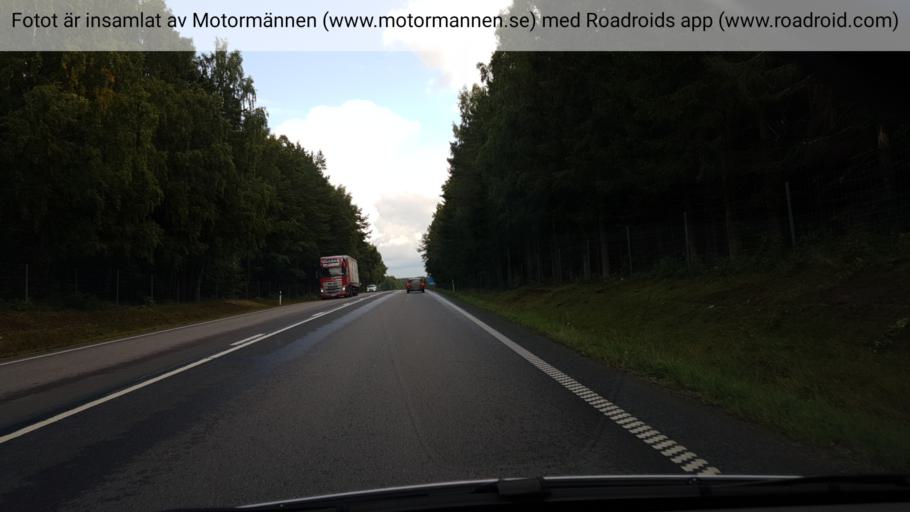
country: SE
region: Vaestra Goetaland
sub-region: Lidkopings Kommun
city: Vinninga
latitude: 58.4405
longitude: 13.2637
